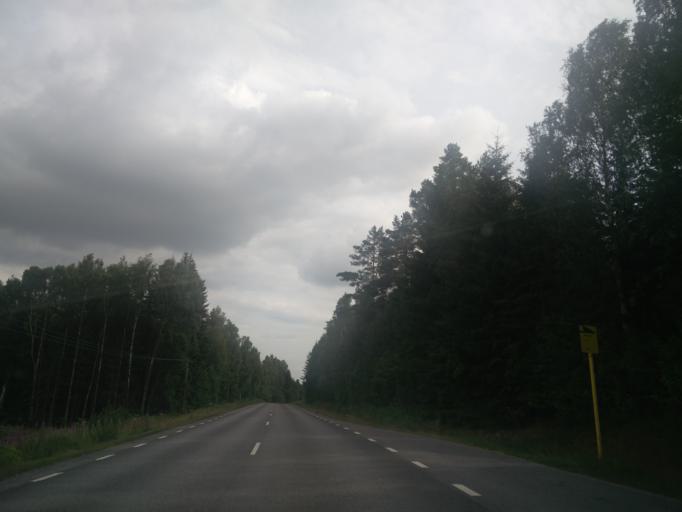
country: SE
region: Vaermland
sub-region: Arvika Kommun
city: Arvika
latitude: 59.7166
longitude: 12.5680
